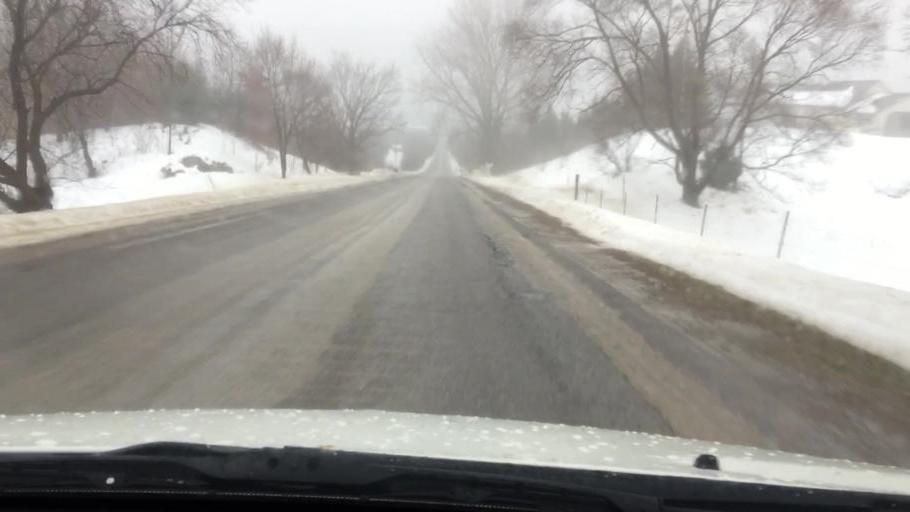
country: US
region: Michigan
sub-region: Charlevoix County
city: East Jordan
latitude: 45.1325
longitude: -85.1578
